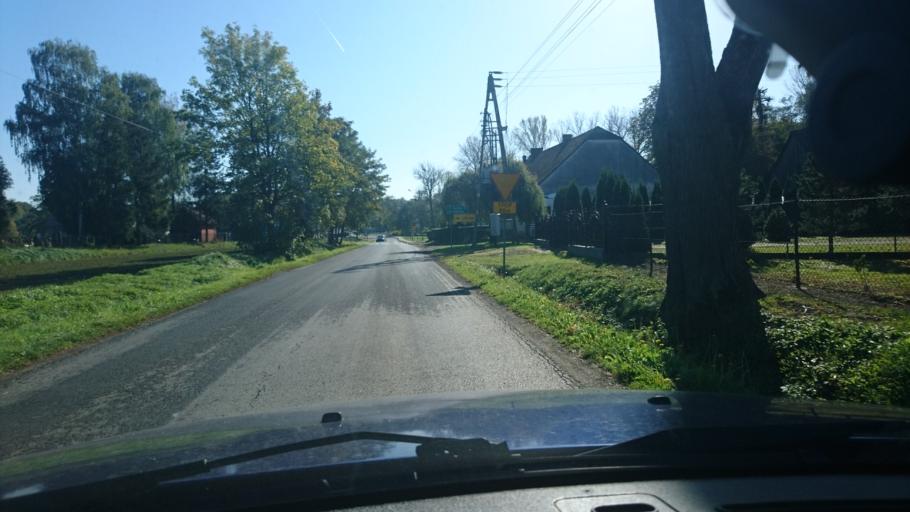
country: PL
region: Silesian Voivodeship
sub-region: Powiat bielski
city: Bronow
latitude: 49.8511
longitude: 18.9393
